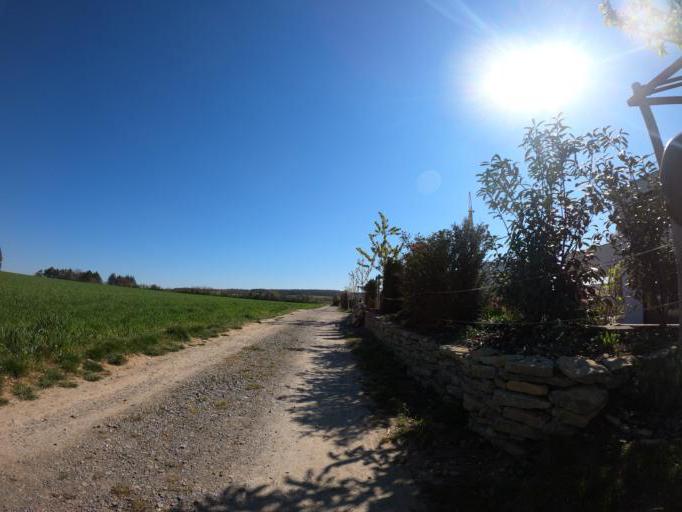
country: DE
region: Baden-Wuerttemberg
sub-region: Karlsruhe Region
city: Monsheim
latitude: 48.8935
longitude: 8.8832
